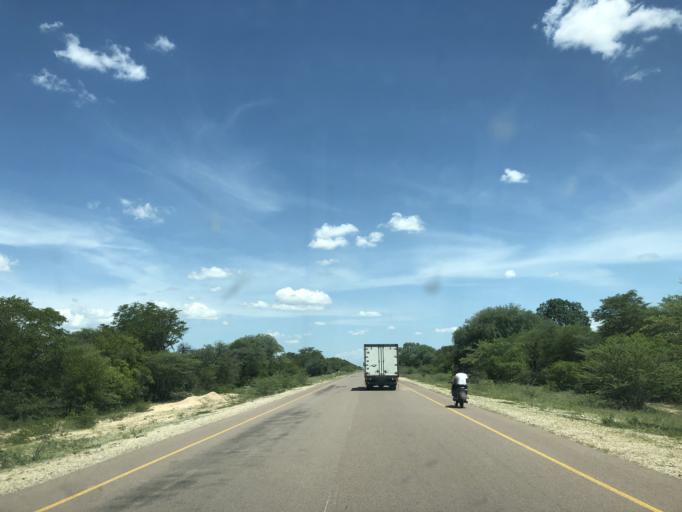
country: AO
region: Cunene
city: Ondjiva
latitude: -16.7857
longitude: 15.4123
